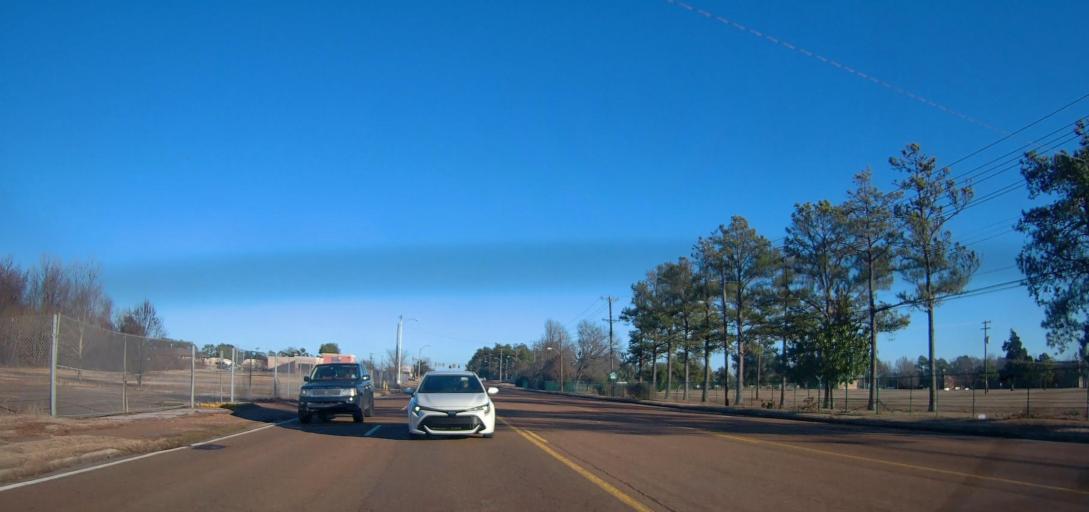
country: US
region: Tennessee
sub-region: Shelby County
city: Millington
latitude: 35.3409
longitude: -89.8805
